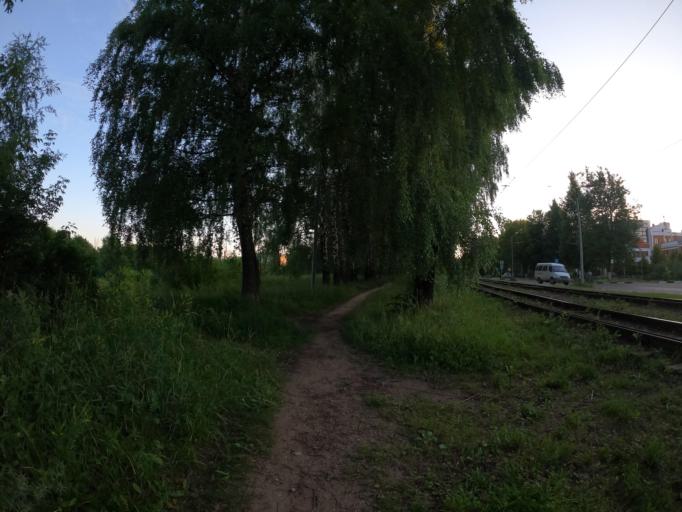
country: RU
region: Moskovskaya
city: Kolomna
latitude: 55.0736
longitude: 38.7941
